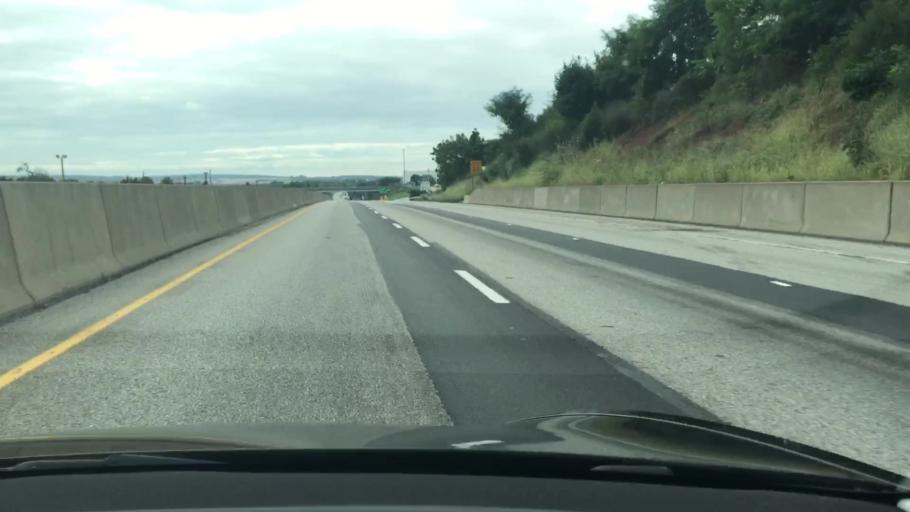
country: US
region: Pennsylvania
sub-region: York County
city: Manchester
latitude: 40.0851
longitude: -76.7676
